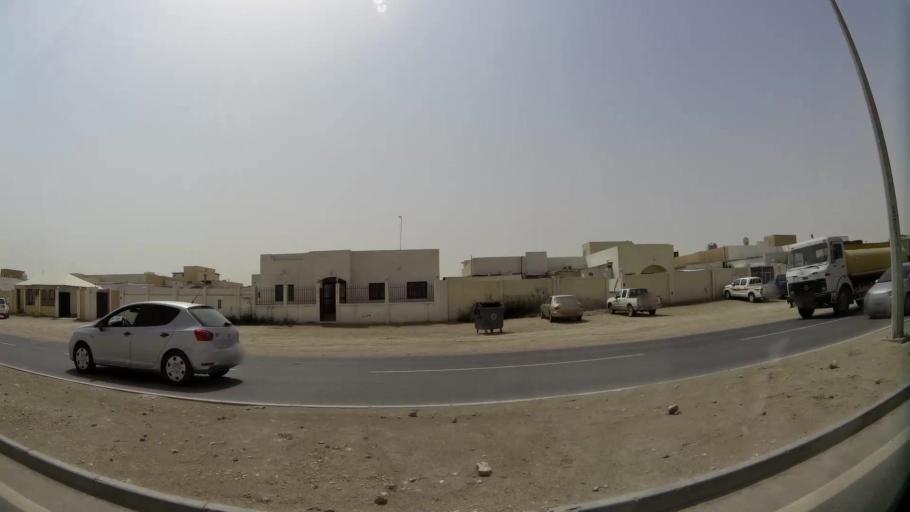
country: QA
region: Baladiyat ar Rayyan
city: Ar Rayyan
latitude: 25.2434
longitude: 51.3792
